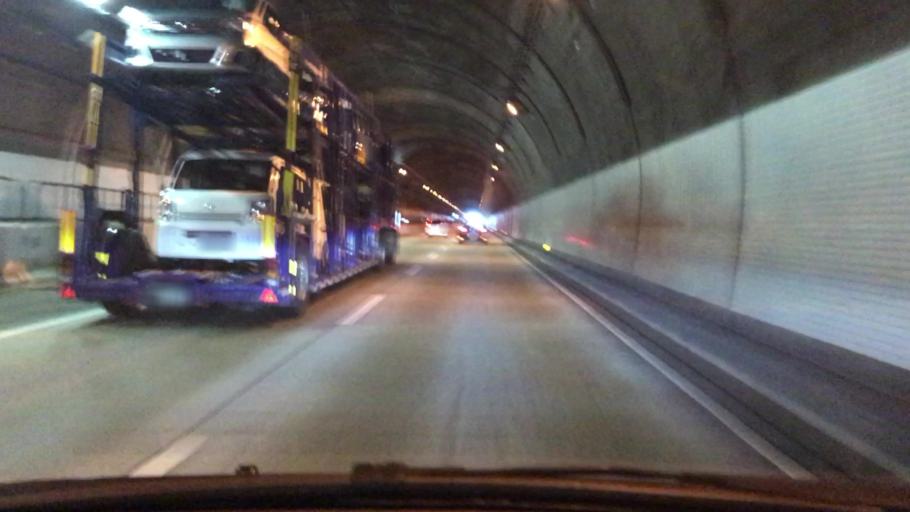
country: JP
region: Hyogo
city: Kobe
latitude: 34.7820
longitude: 135.2136
